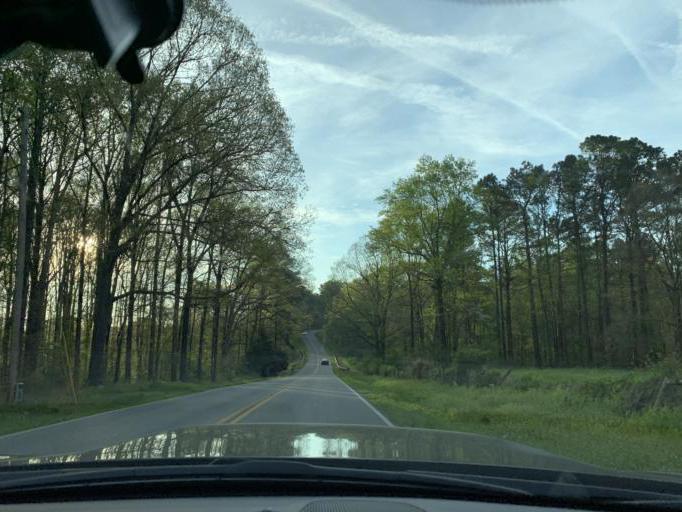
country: US
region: Georgia
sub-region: Forsyth County
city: Cumming
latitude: 34.2594
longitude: -84.1506
